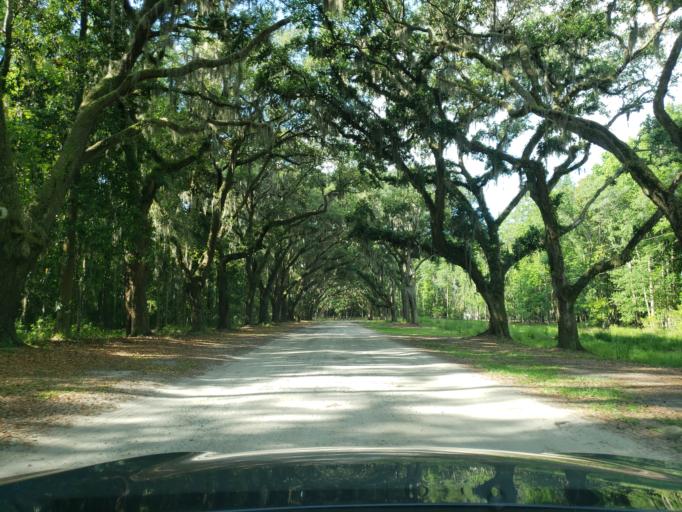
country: US
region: Georgia
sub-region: Chatham County
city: Isle of Hope
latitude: 31.9644
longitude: -81.0693
